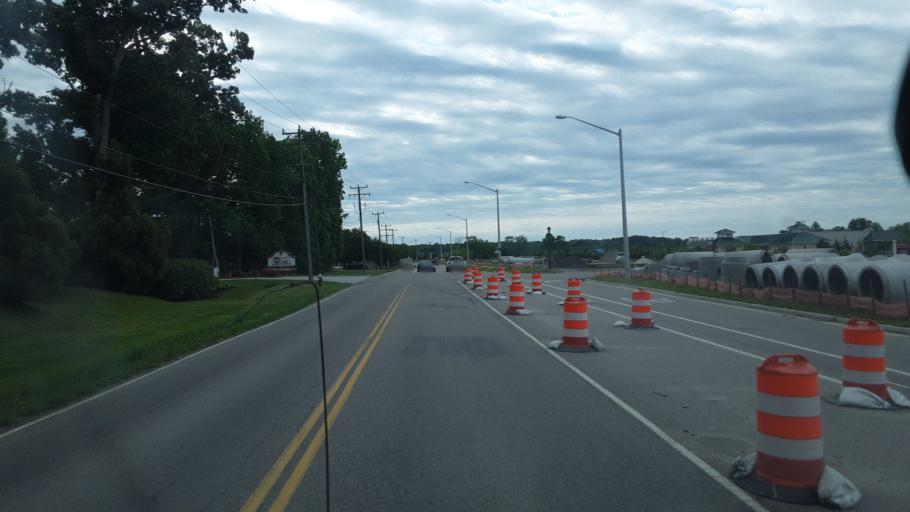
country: US
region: Virginia
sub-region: City of Virginia Beach
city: Virginia Beach
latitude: 36.7493
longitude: -76.0066
